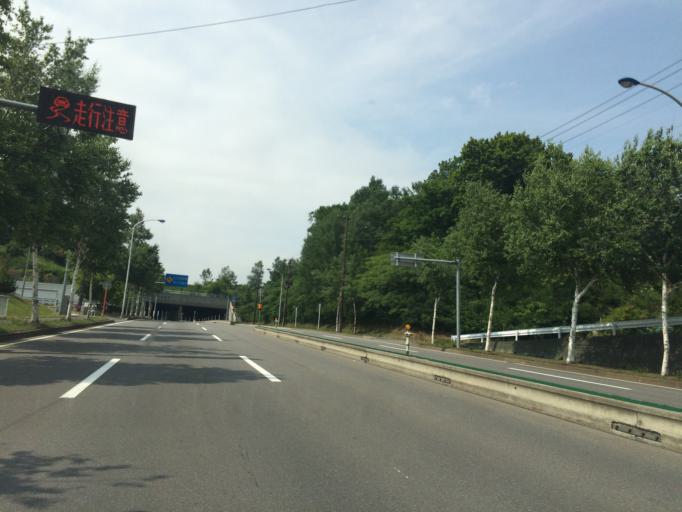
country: JP
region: Hokkaido
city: Sapporo
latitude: 43.0802
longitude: 141.2671
